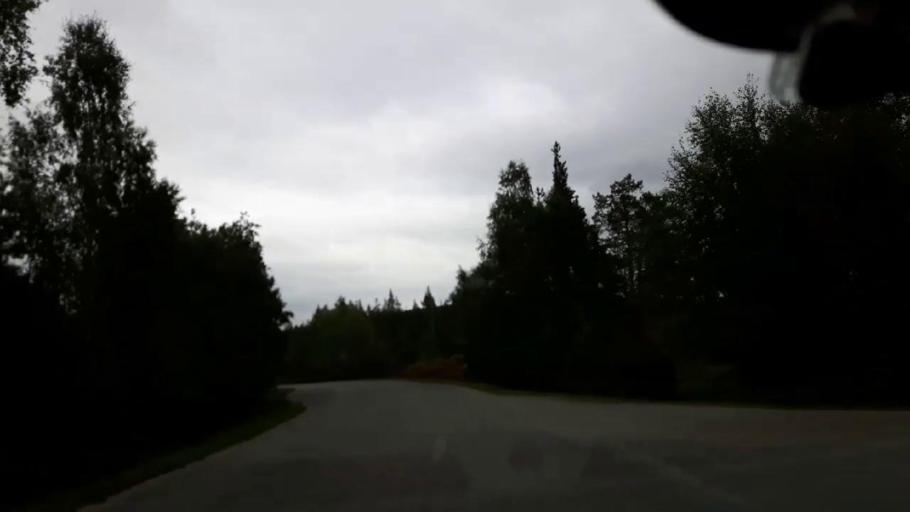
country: SE
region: Vaesternorrland
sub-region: Ange Kommun
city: Fransta
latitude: 62.7759
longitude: 16.2272
